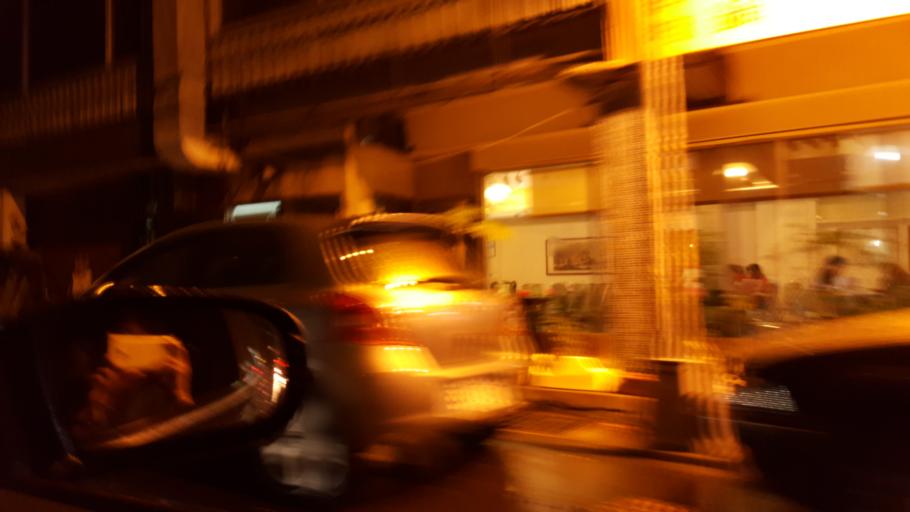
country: TW
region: Taiwan
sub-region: Hsinchu
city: Zhubei
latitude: 24.8291
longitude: 121.0068
